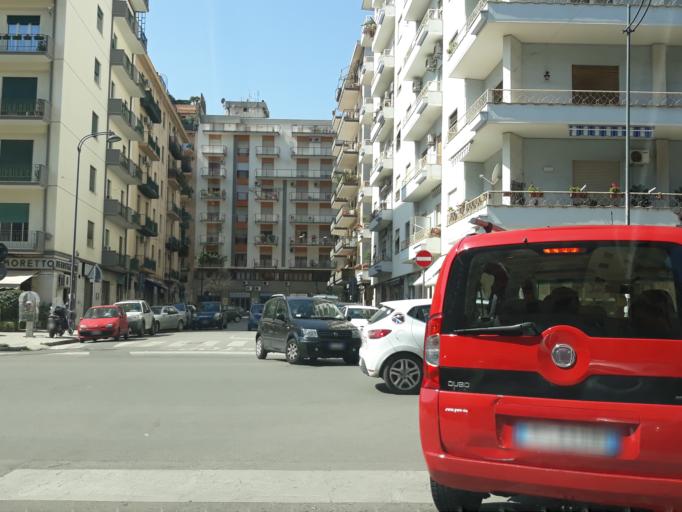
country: IT
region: Sicily
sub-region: Palermo
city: Palermo
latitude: 38.1353
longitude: 13.3520
